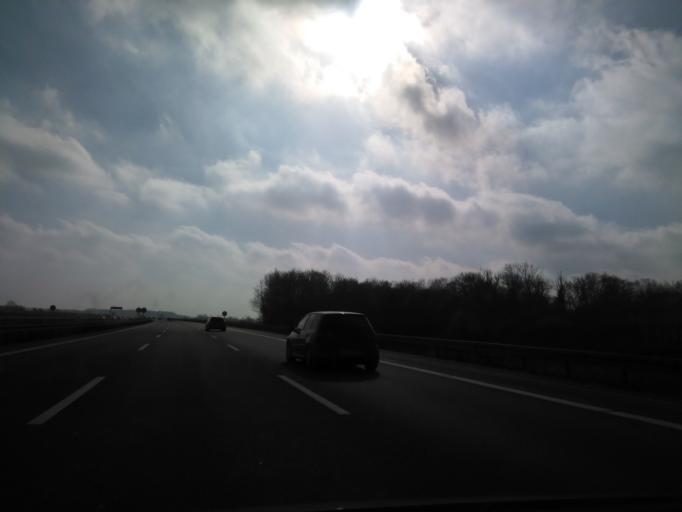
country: DK
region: South Denmark
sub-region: Vejle Kommune
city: Borkop
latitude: 55.6281
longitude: 9.5667
